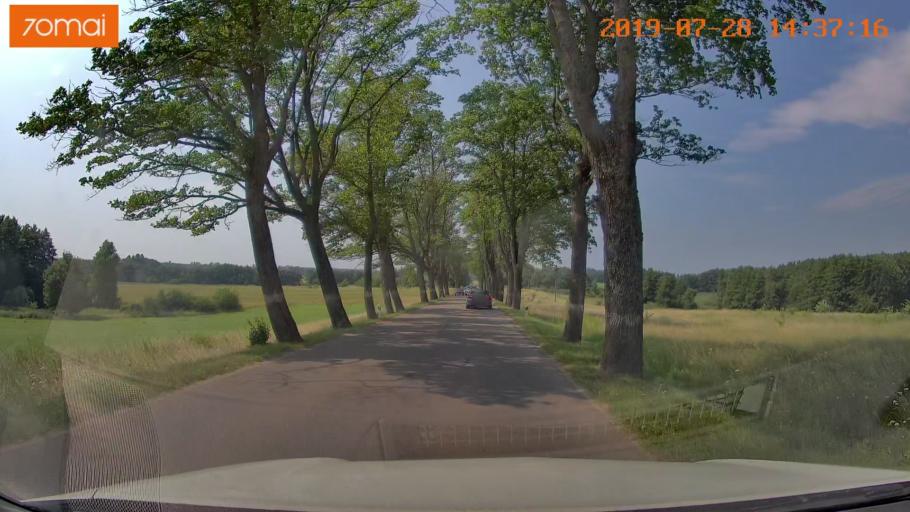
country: RU
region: Kaliningrad
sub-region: Gorod Kaliningrad
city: Yantarnyy
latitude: 54.8404
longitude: 20.0007
